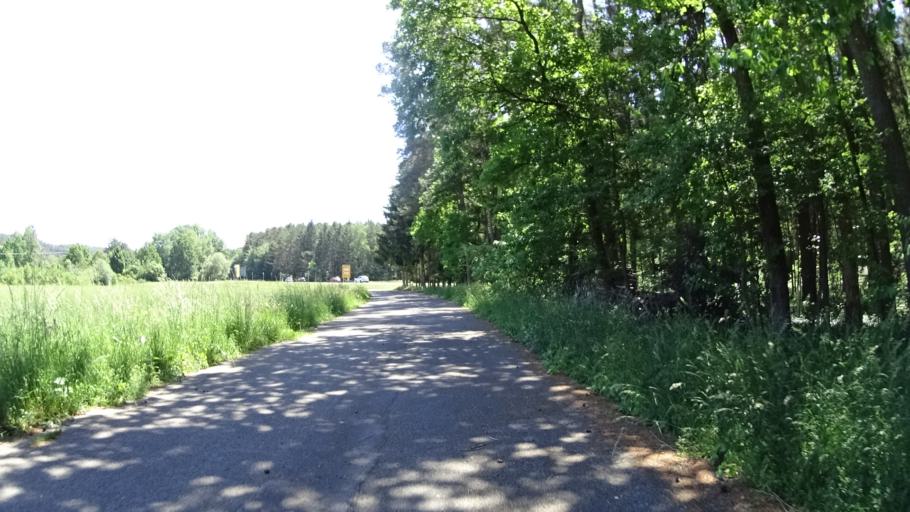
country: DE
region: Bavaria
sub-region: Regierungsbezirk Mittelfranken
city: Absberg
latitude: 49.1092
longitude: 10.9231
